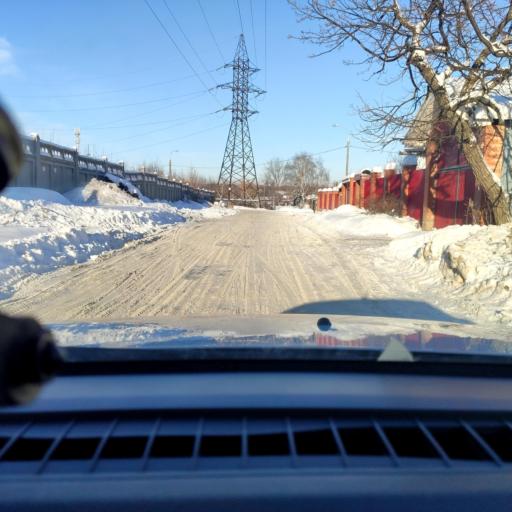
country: RU
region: Samara
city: Petra-Dubrava
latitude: 53.3110
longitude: 50.2970
